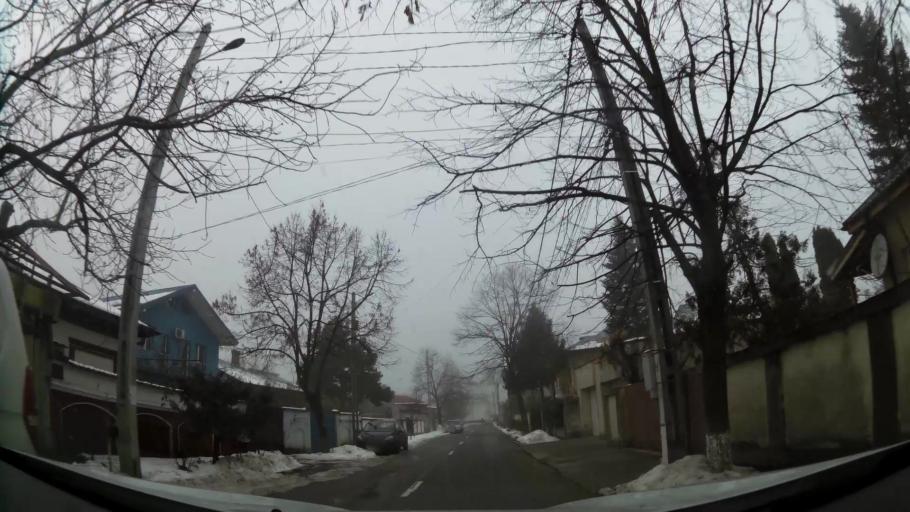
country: RO
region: Ilfov
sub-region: Comuna Chiajna
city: Chiajna
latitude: 44.4627
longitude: 25.9783
